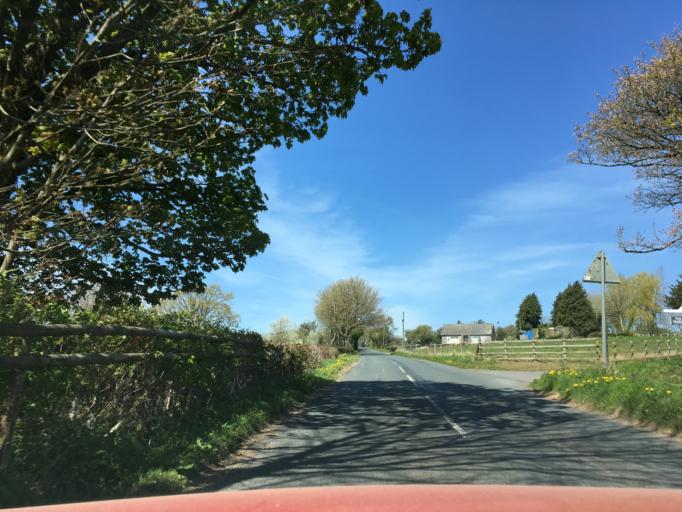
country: GB
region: Wales
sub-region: Newport
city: Llanvaches
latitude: 51.6481
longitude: -2.7760
